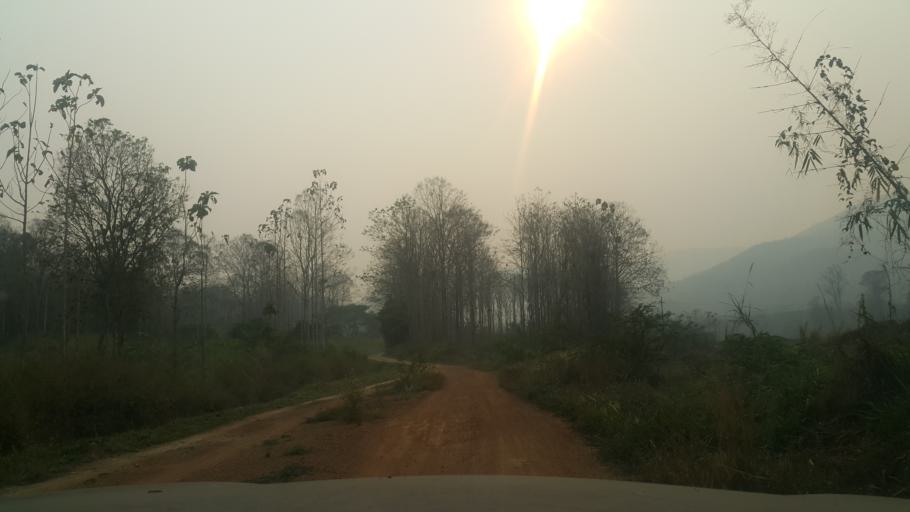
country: TH
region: Lamphun
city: Mae Tha
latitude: 18.5083
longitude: 99.2148
